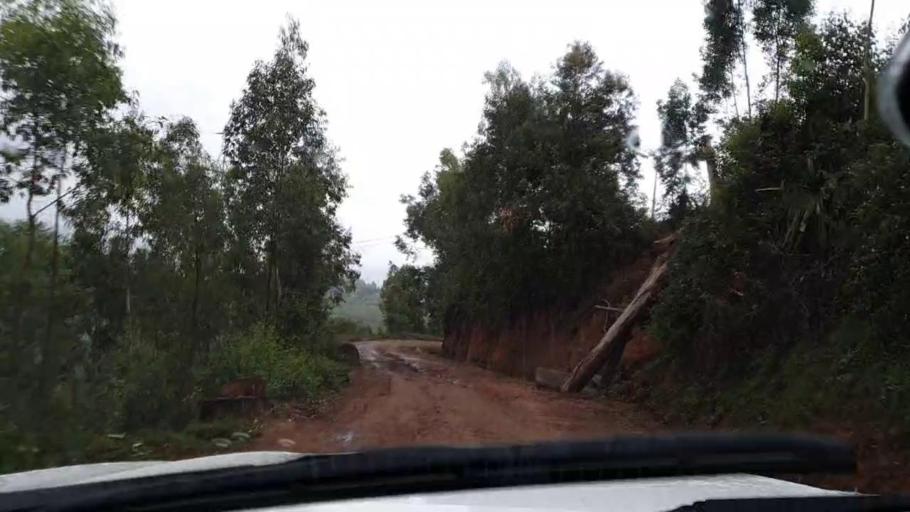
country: BI
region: Kayanza
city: Kayanza
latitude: -2.7831
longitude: 29.5331
